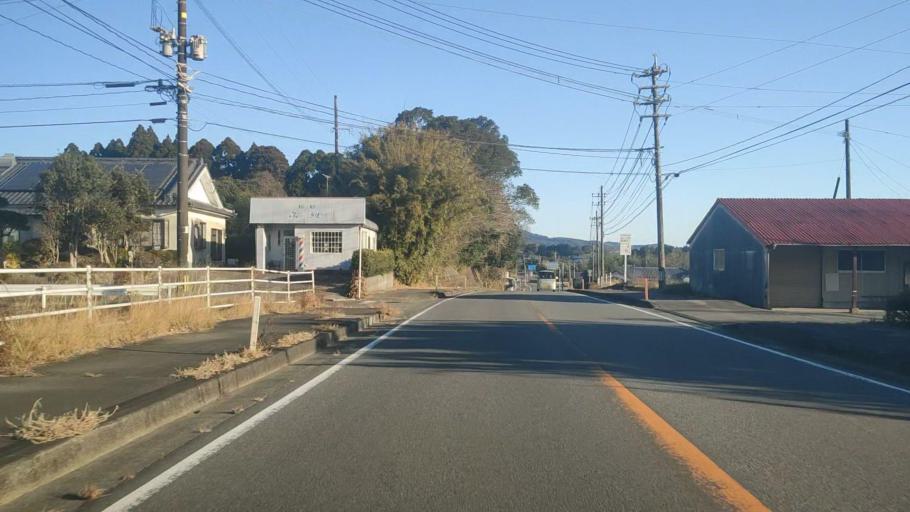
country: JP
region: Miyazaki
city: Takanabe
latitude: 32.3051
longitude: 131.5826
